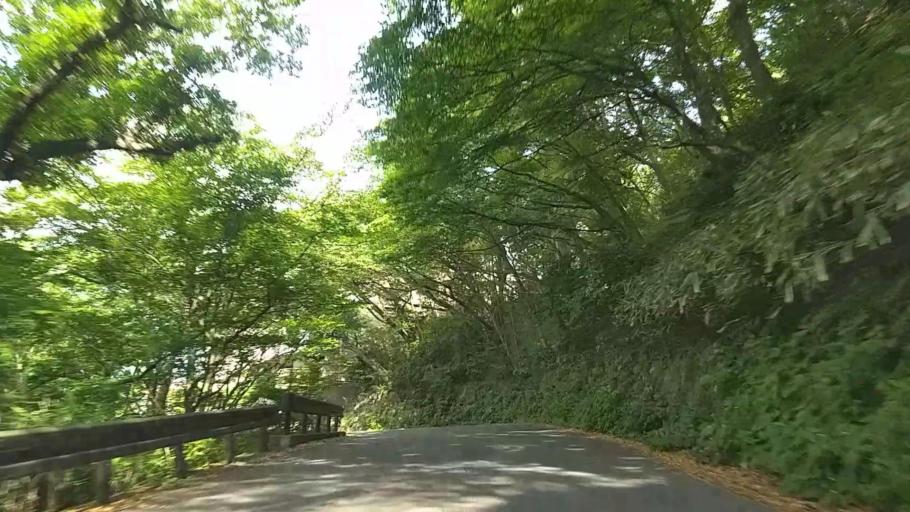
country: JP
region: Kanagawa
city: Hakone
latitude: 35.2520
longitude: 139.0376
